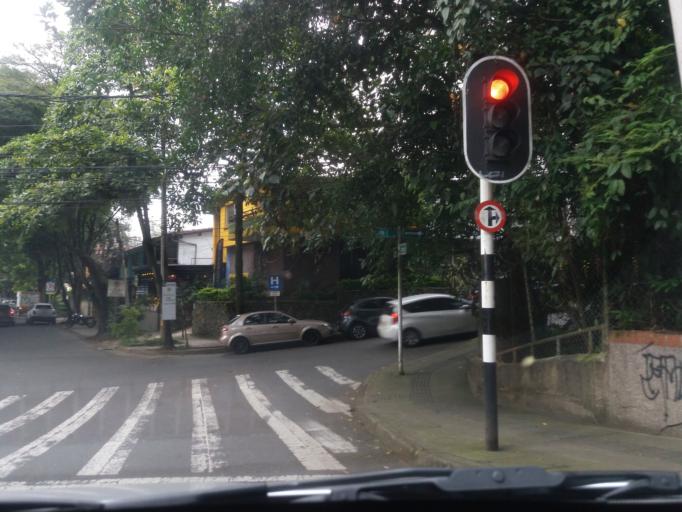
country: CO
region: Antioquia
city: Envigado
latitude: 6.1920
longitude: -75.5772
